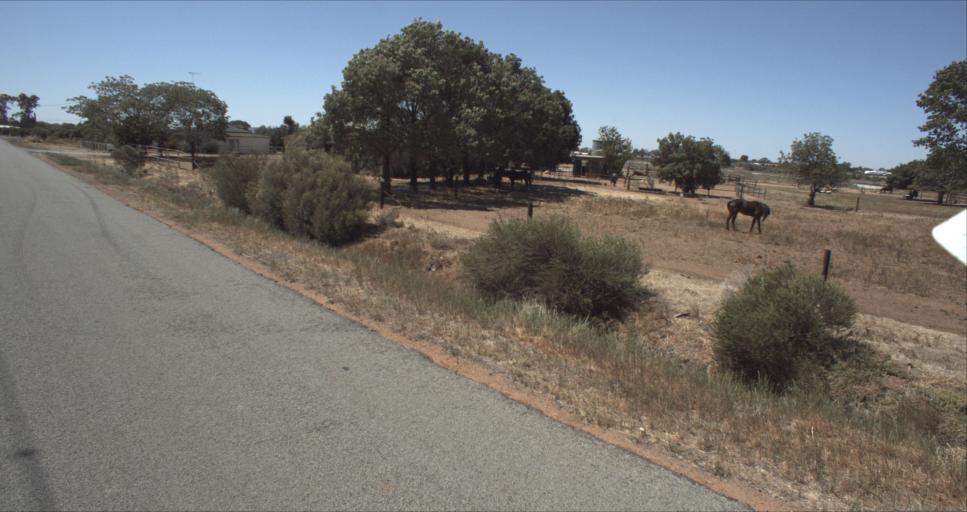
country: AU
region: New South Wales
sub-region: Leeton
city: Leeton
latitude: -34.5357
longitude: 146.3973
